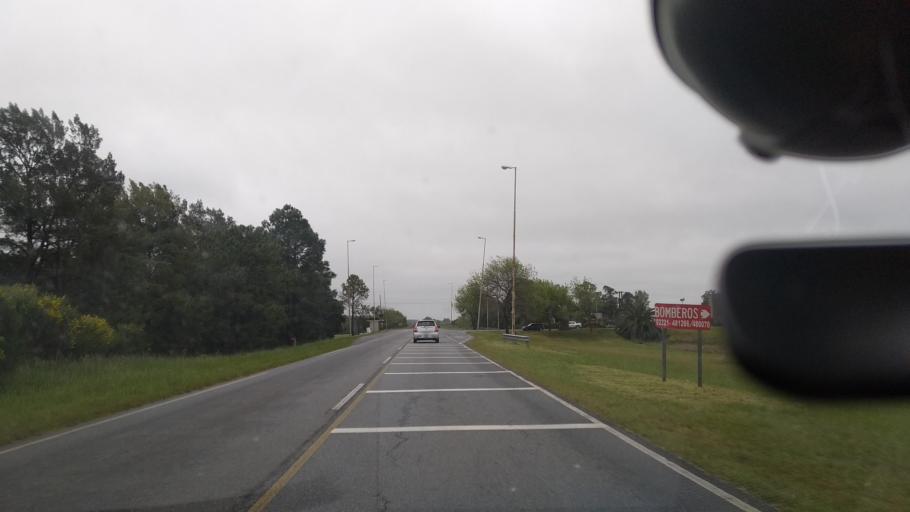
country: AR
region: Buenos Aires
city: Veronica
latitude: -35.4011
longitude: -57.3533
